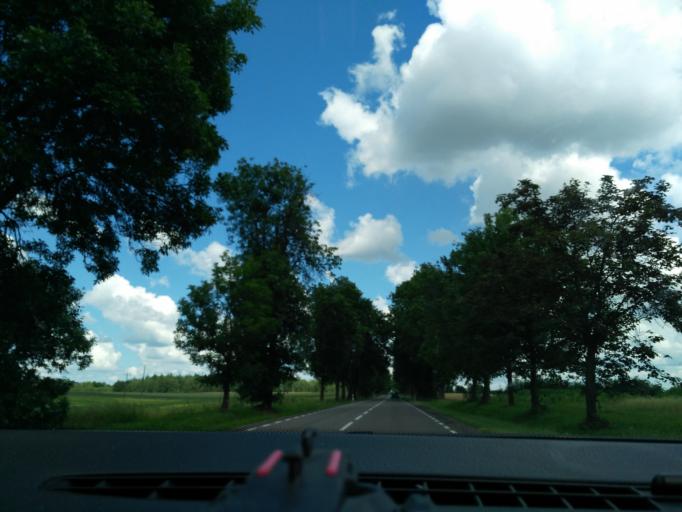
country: PL
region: Podlasie
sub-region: Powiat bielski
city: Bielsk Podlaski
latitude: 52.8220
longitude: 23.1954
